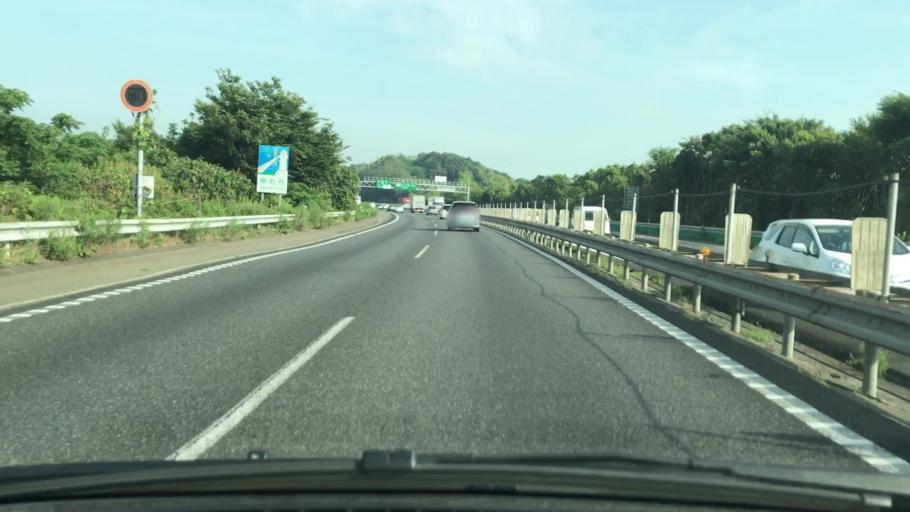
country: JP
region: Hyogo
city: Akashi
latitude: 34.6977
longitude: 134.9669
